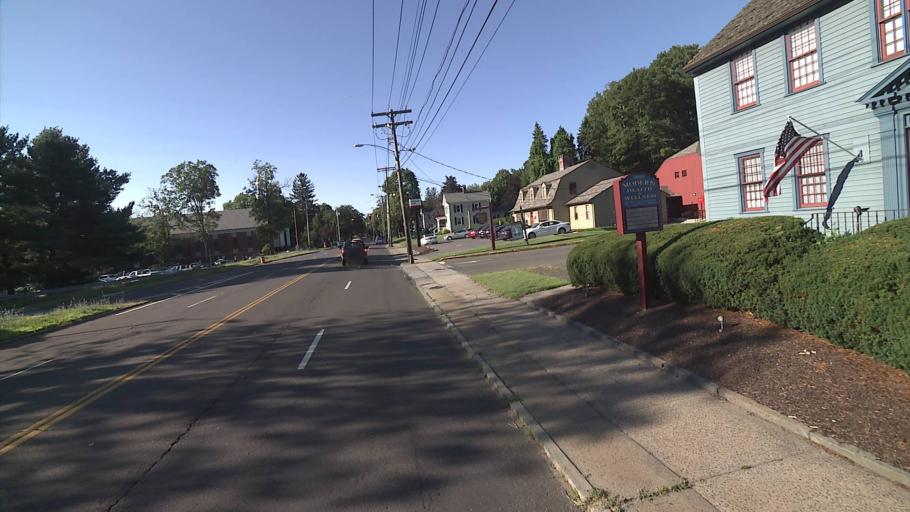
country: US
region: Connecticut
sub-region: New Haven County
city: Hamden
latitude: 41.4003
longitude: -72.8976
